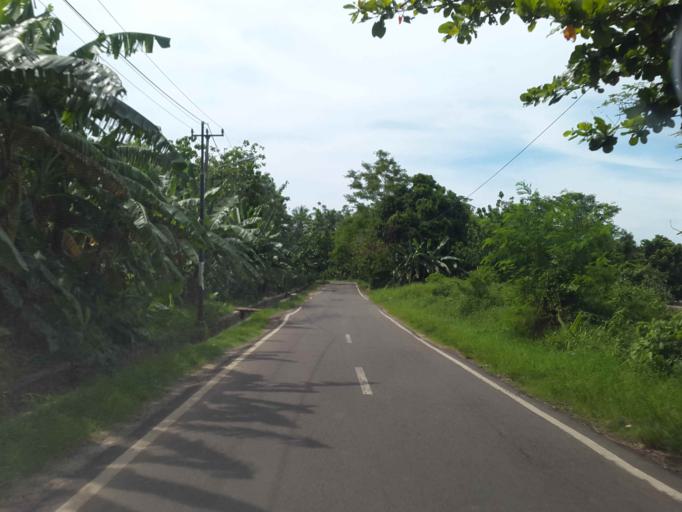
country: ID
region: Banten
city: Citeureup
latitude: -6.5275
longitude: 105.7047
